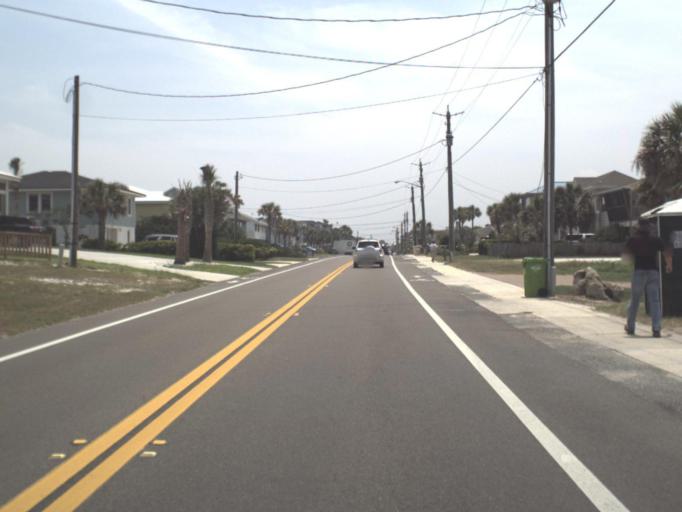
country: US
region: Florida
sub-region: Nassau County
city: Fernandina Beach
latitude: 30.6435
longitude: -81.4358
